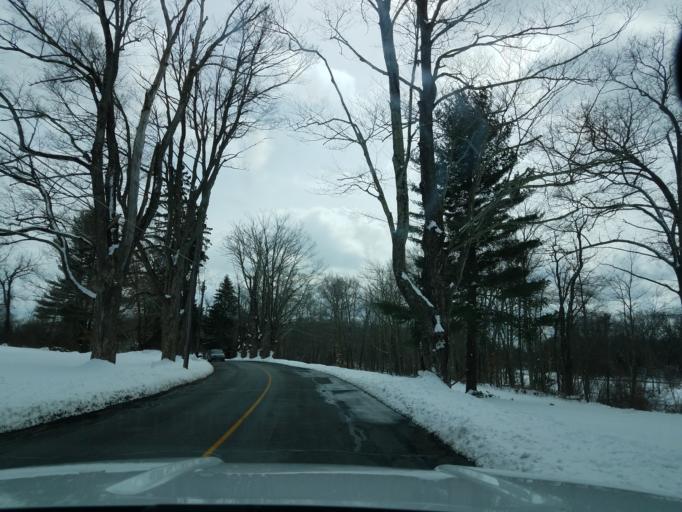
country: US
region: Connecticut
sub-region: Litchfield County
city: Litchfield
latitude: 41.7214
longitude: -73.2216
